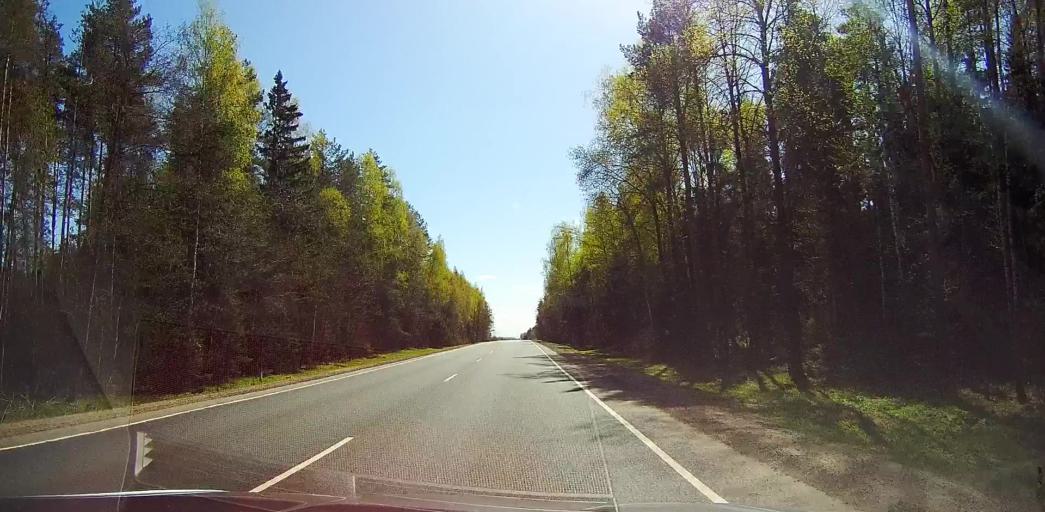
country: RU
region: Moskovskaya
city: Gzhel'
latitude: 55.6027
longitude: 38.3775
